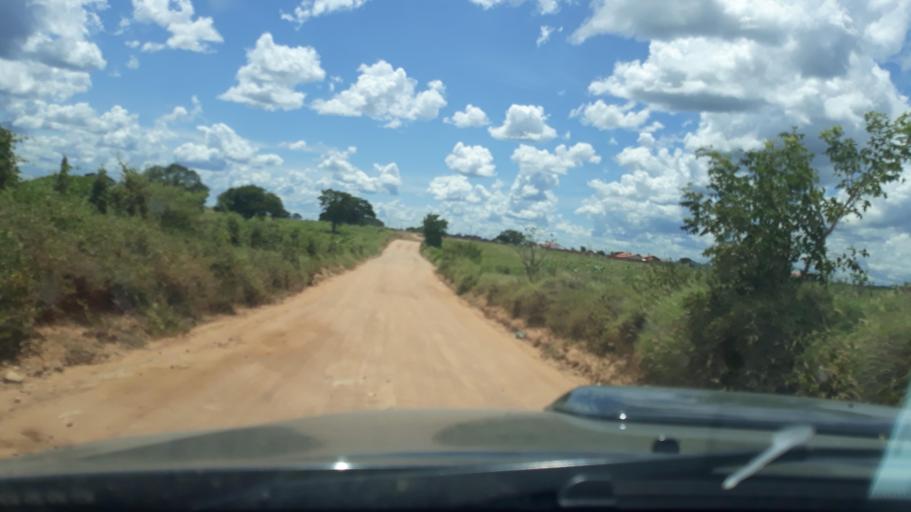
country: BR
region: Bahia
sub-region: Riacho De Santana
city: Riacho de Santana
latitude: -13.9080
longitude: -42.8532
